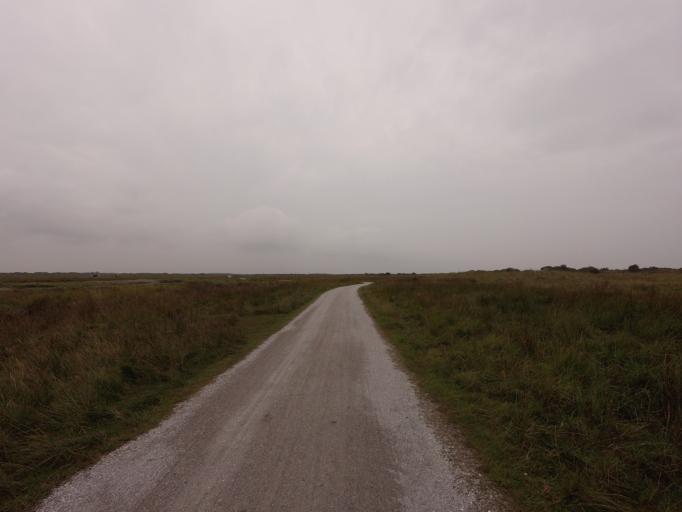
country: NL
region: Friesland
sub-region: Gemeente Schiermonnikoog
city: Schiermonnikoog
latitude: 53.4869
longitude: 6.2129
